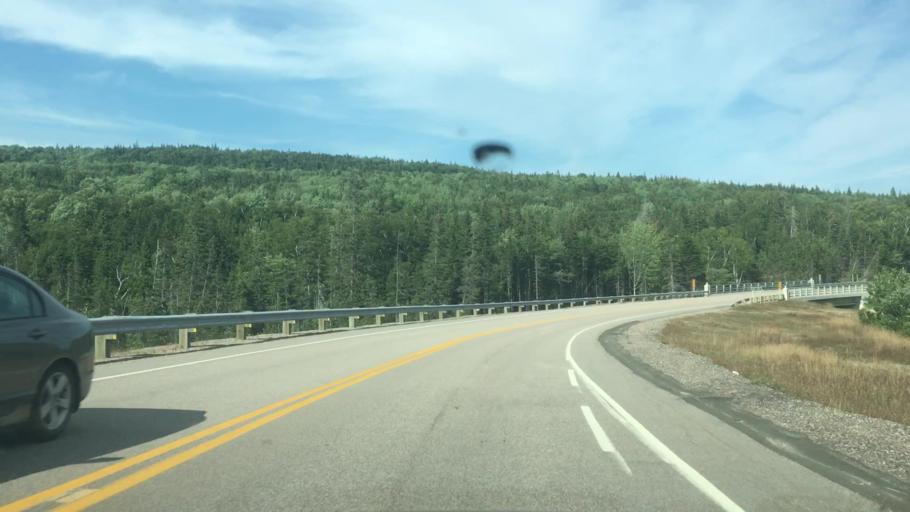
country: CA
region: Nova Scotia
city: Sydney Mines
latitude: 46.7113
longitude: -60.3682
